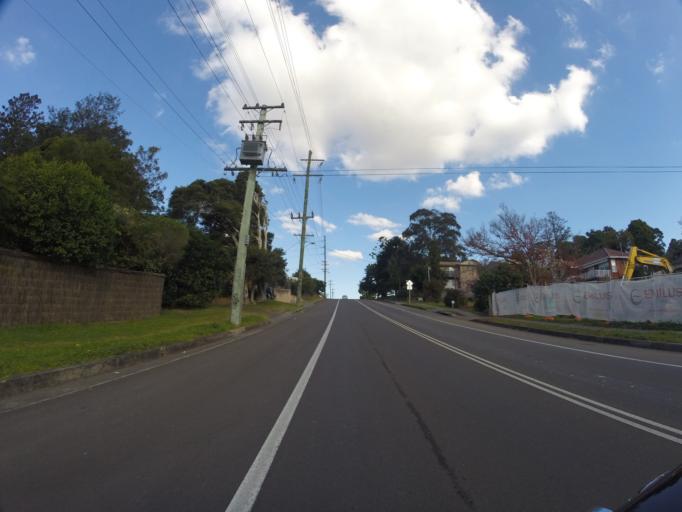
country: AU
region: New South Wales
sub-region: Wollongong
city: Keiraville
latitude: -34.4191
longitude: 150.8695
